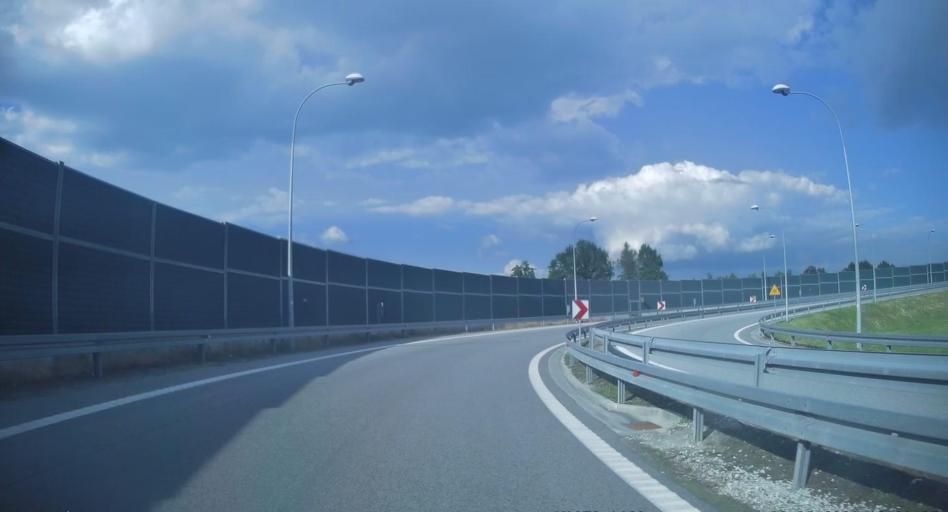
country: PL
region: Subcarpathian Voivodeship
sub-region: Powiat debicki
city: Zyrakow
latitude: 50.0800
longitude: 21.3835
